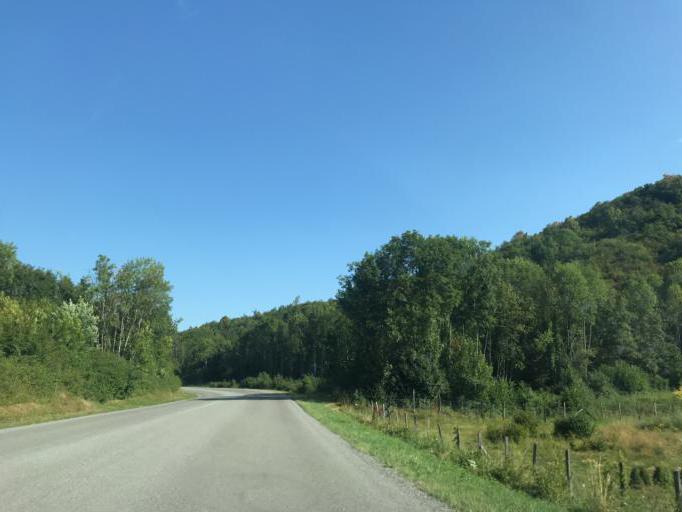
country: FR
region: Franche-Comte
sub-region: Departement du Jura
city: Lavans-les-Saint-Claude
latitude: 46.3796
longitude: 5.7538
